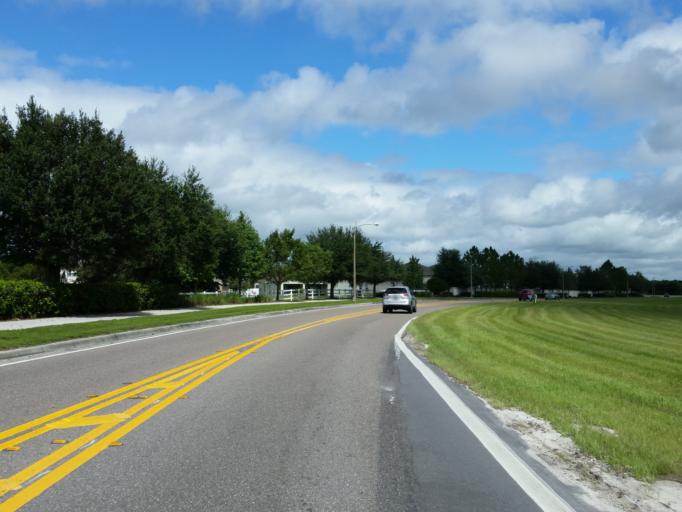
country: US
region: Florida
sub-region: Pasco County
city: Wesley Chapel
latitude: 28.2053
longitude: -82.3005
